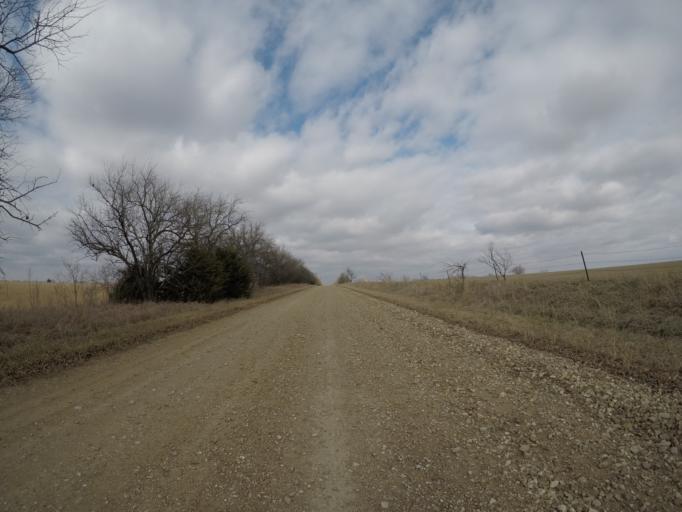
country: US
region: Kansas
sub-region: Morris County
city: Council Grove
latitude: 38.7832
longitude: -96.3527
